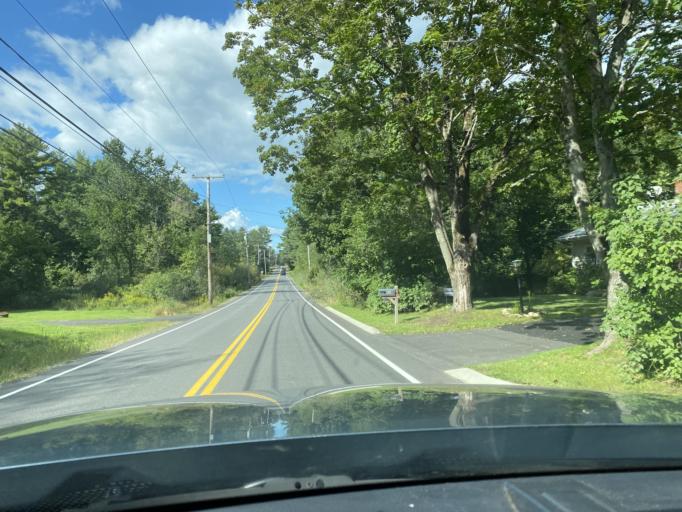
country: US
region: Maine
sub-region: York County
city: Kittery
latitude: 43.1513
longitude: -70.7121
